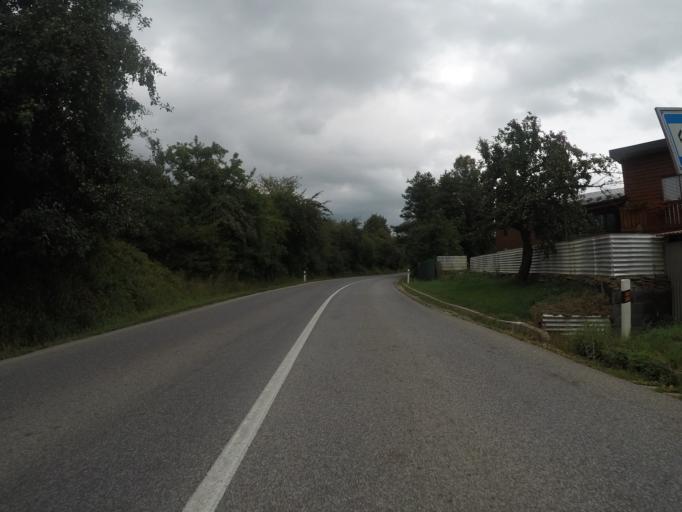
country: SK
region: Kosicky
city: Spisska Nova Ves
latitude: 48.9234
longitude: 20.5403
